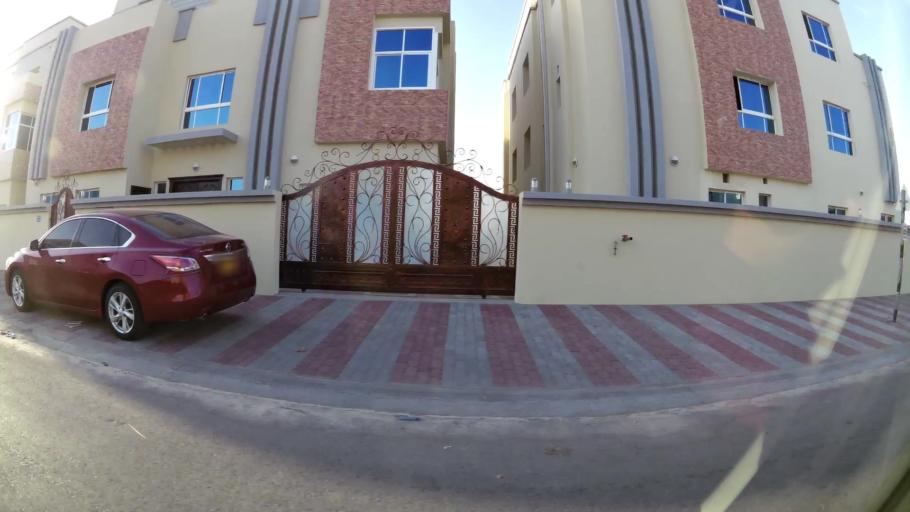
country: OM
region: Muhafazat Masqat
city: As Sib al Jadidah
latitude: 23.5916
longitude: 58.1367
